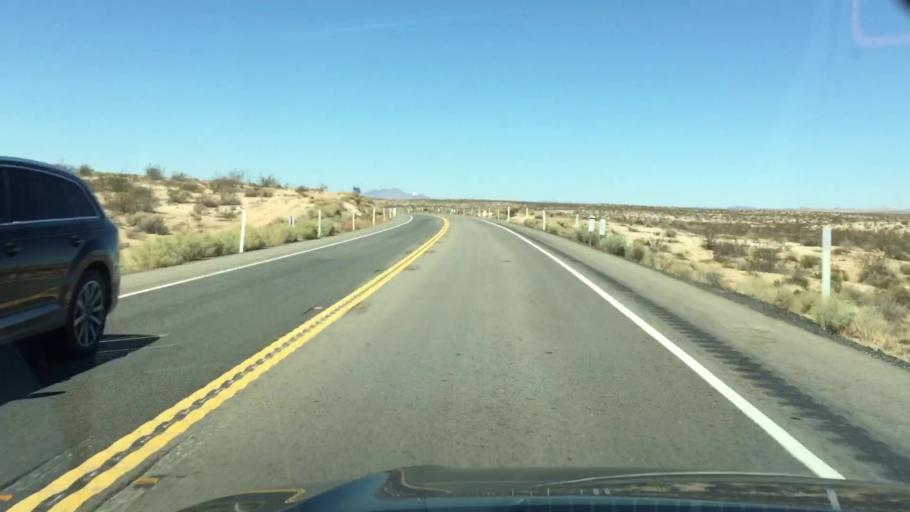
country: US
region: California
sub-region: Kern County
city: Boron
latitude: 35.0689
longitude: -117.5591
